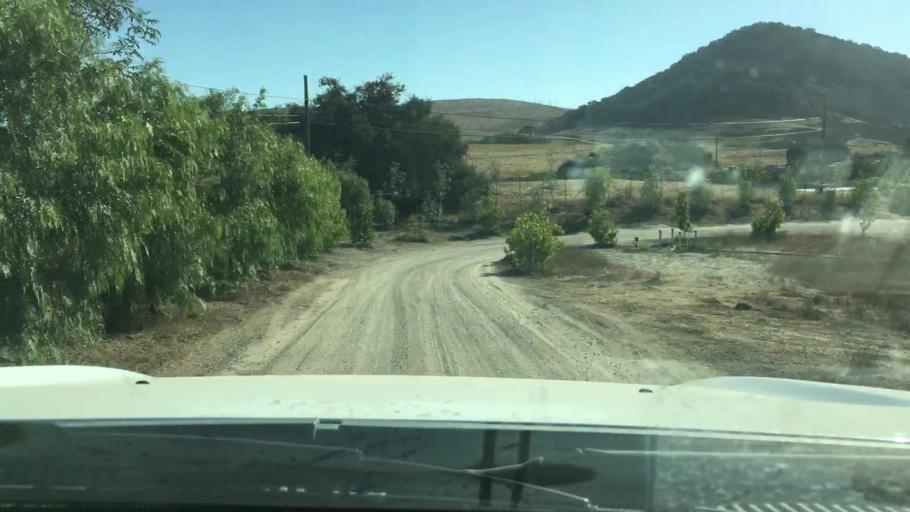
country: US
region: California
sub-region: San Luis Obispo County
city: Arroyo Grande
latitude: 35.1049
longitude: -120.5537
